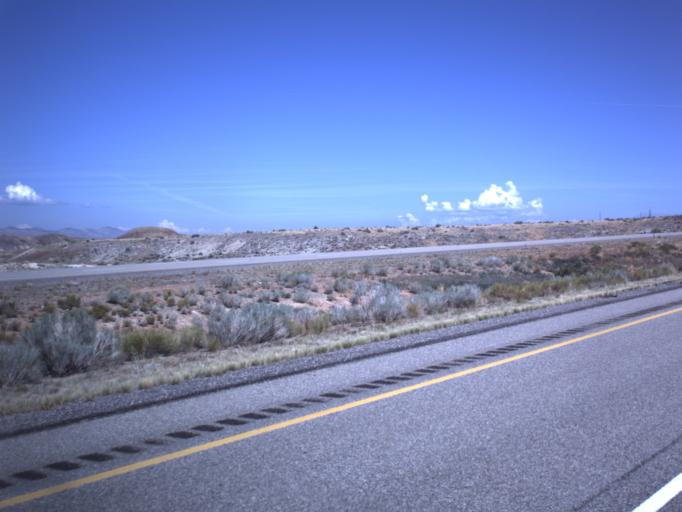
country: US
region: Utah
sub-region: Sevier County
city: Salina
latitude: 38.9211
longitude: -111.8765
